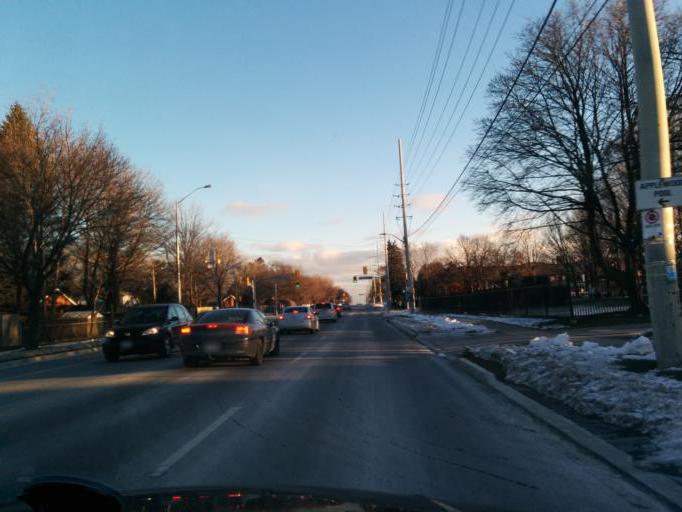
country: CA
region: Ontario
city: Etobicoke
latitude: 43.6058
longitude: -79.6010
